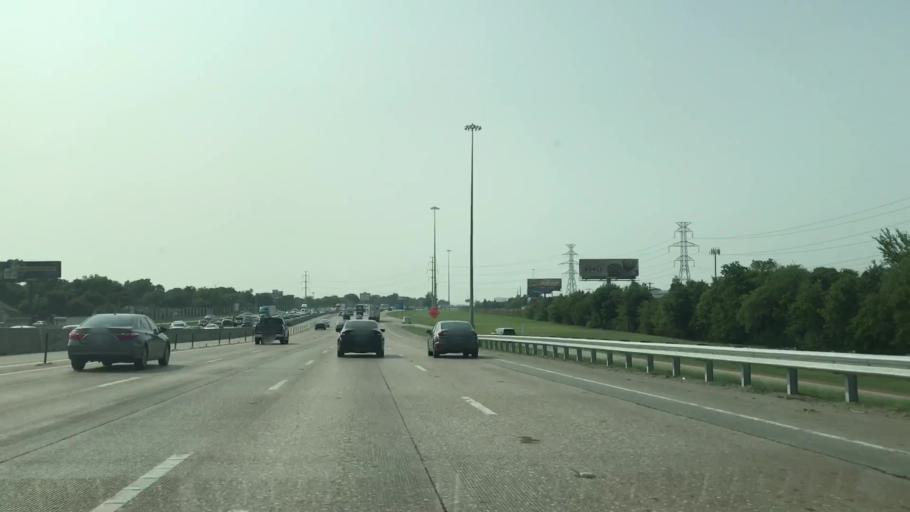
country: US
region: Texas
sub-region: Dallas County
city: Richardson
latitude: 32.8840
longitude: -96.7047
